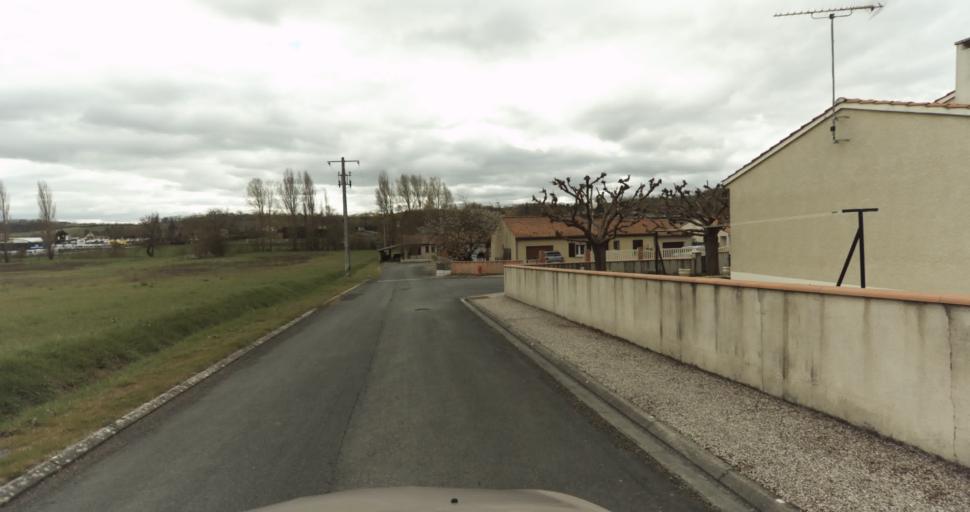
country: FR
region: Midi-Pyrenees
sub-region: Departement du Tarn
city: Puygouzon
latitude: 43.8987
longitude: 2.1533
